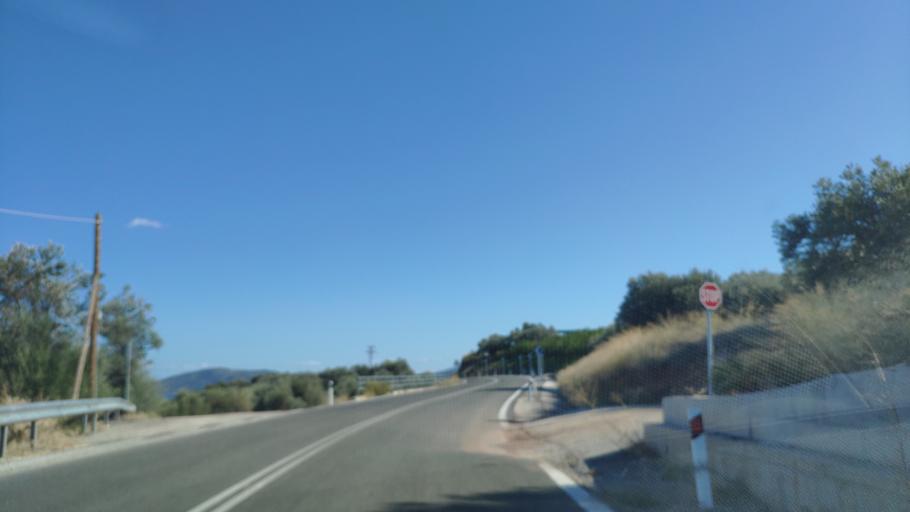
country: GR
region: Peloponnese
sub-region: Nomos Argolidos
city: Didyma
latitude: 37.5499
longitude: 23.2794
